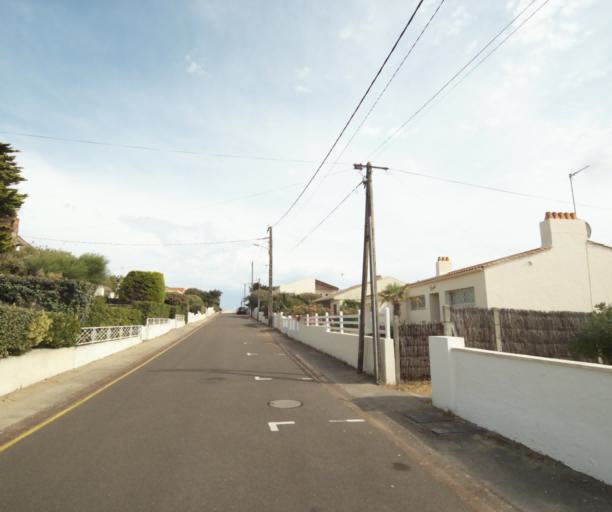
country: FR
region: Pays de la Loire
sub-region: Departement de la Vendee
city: Chateau-d'Olonne
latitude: 46.4771
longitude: -1.7572
